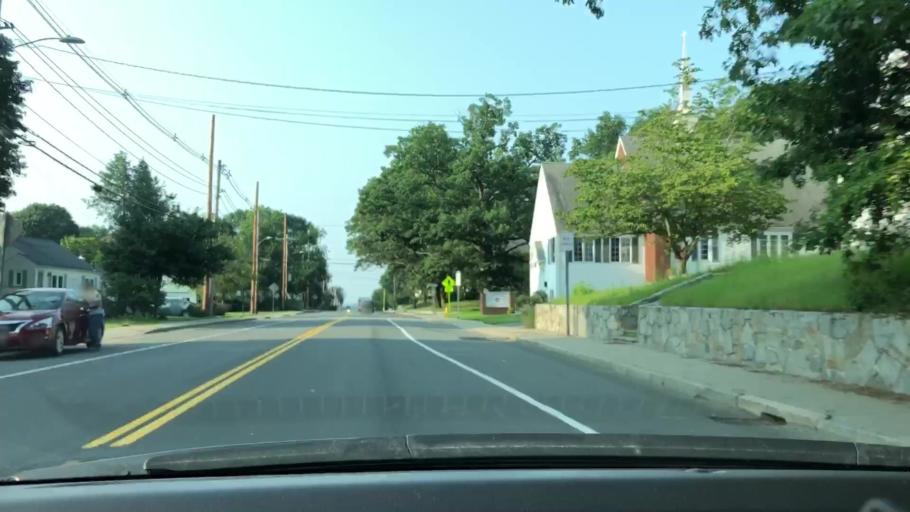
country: US
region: Massachusetts
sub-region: Norfolk County
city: Dedham
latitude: 42.2275
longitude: -71.1864
